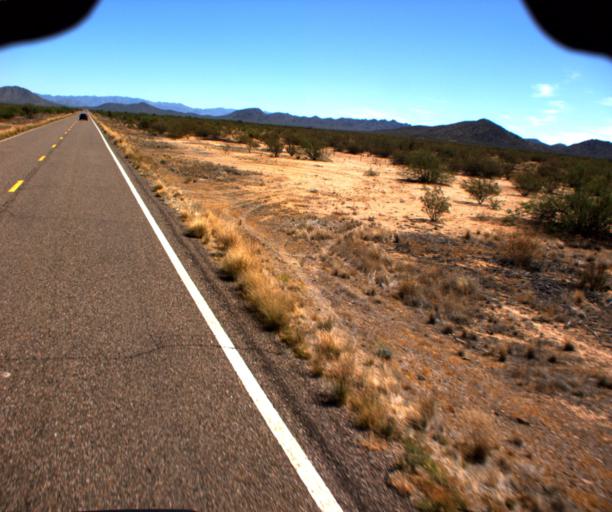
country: US
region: Arizona
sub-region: Yavapai County
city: Congress
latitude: 34.0431
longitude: -113.0676
